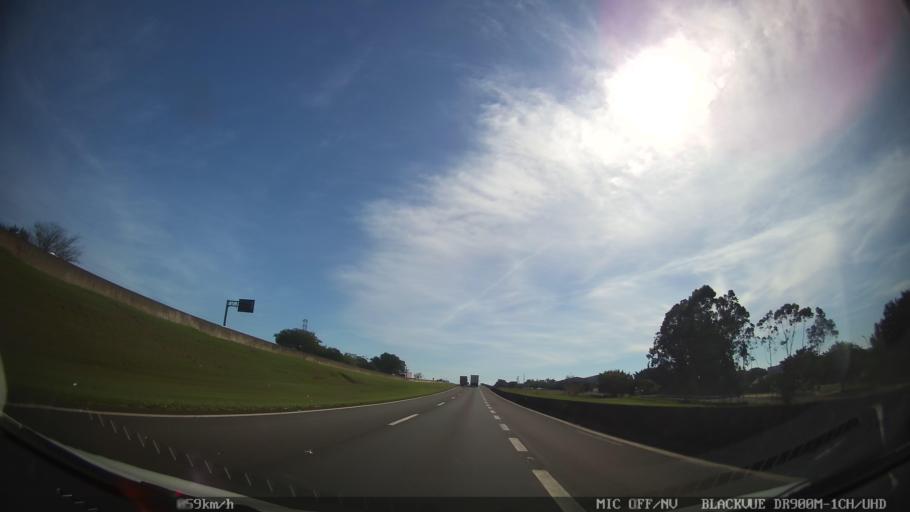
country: BR
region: Sao Paulo
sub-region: Leme
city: Leme
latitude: -22.1873
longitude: -47.3980
